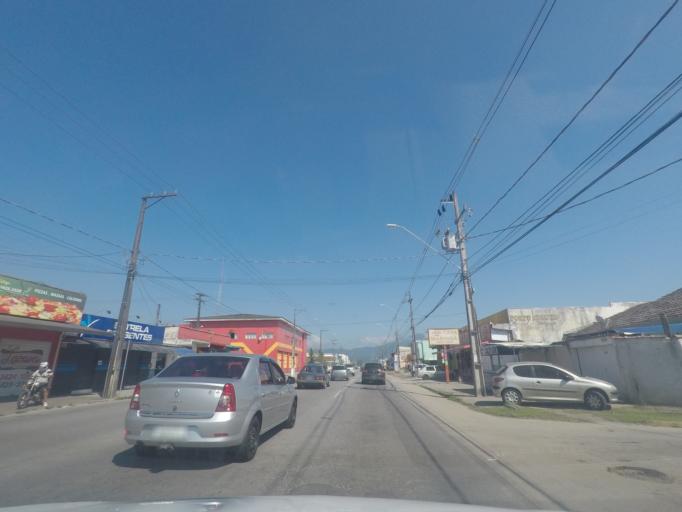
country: BR
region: Parana
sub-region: Paranagua
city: Paranagua
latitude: -25.5628
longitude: -48.5645
